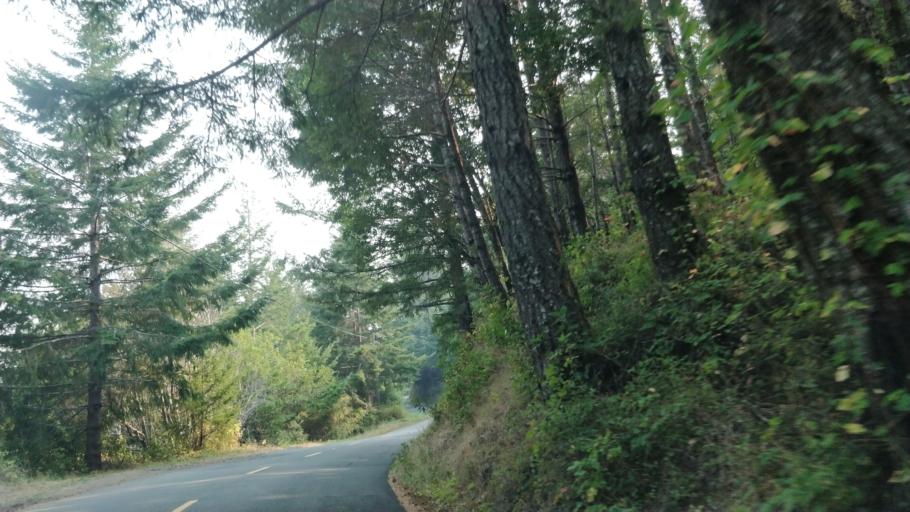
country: US
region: California
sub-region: Humboldt County
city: Rio Dell
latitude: 40.2961
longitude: -124.2503
